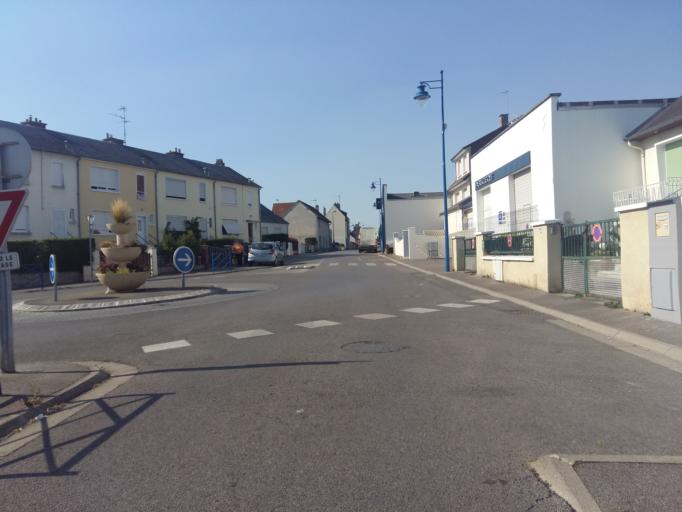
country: FR
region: Picardie
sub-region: Departement de la Somme
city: Rivery
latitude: 49.9050
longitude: 2.3216
